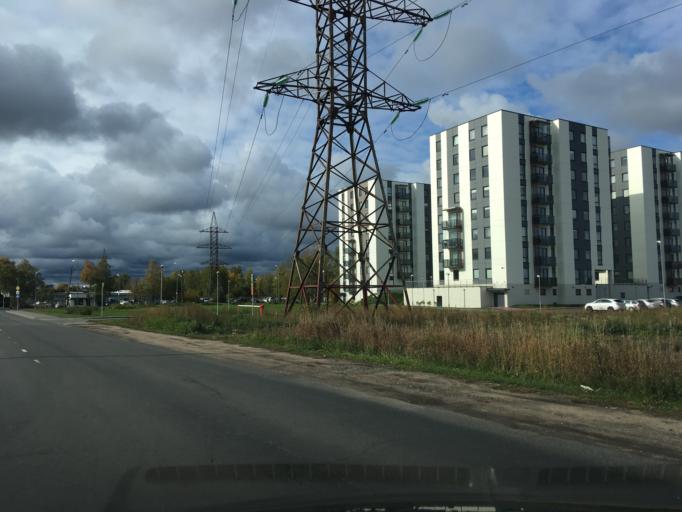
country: EE
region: Harju
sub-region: Tallinna linn
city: Kose
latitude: 59.4435
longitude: 24.8314
